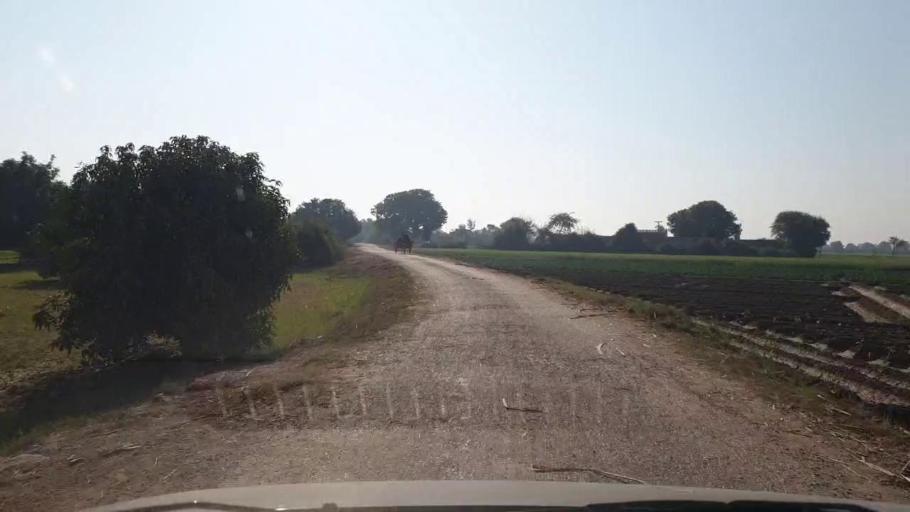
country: PK
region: Sindh
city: Tando Jam
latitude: 25.4310
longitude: 68.6043
